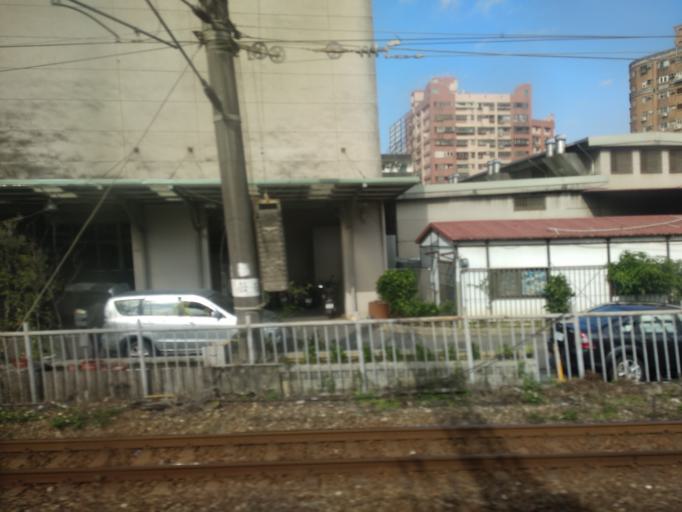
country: TW
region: Taipei
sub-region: Taipei
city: Banqiao
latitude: 24.9877
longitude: 121.4225
